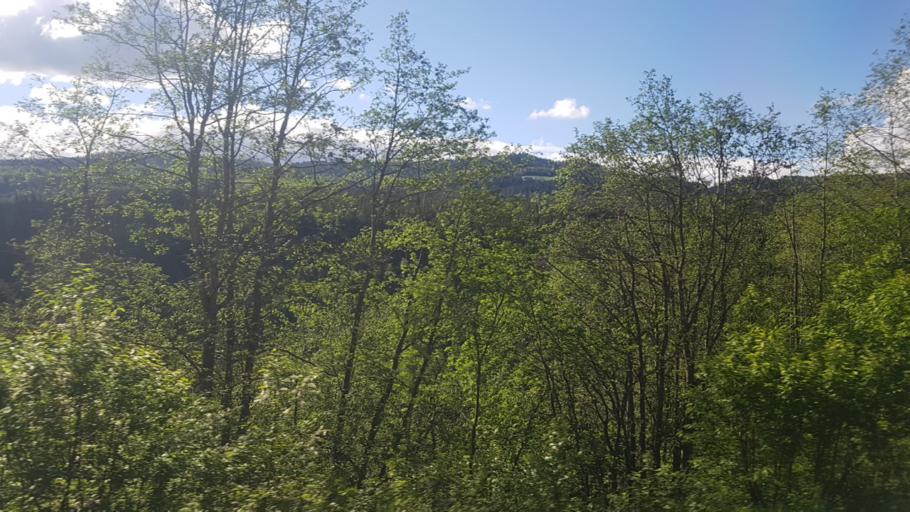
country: NO
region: Sor-Trondelag
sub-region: Midtre Gauldal
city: Storen
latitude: 62.9716
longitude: 10.2078
